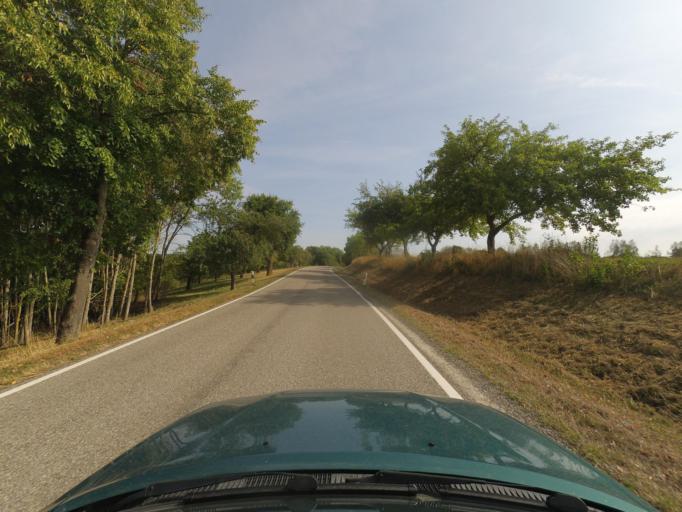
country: DE
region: Bavaria
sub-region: Regierungsbezirk Mittelfranken
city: Lichtenau
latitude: 49.1962
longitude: 10.3925
